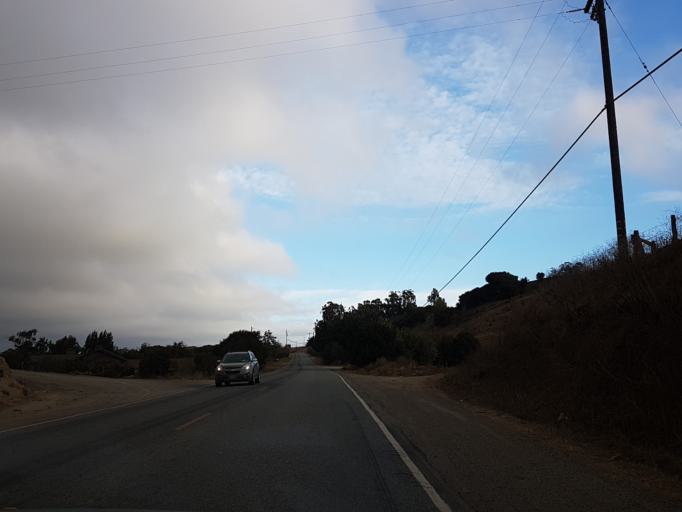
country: US
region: California
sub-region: Monterey County
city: Salinas
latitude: 36.5944
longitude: -121.6166
